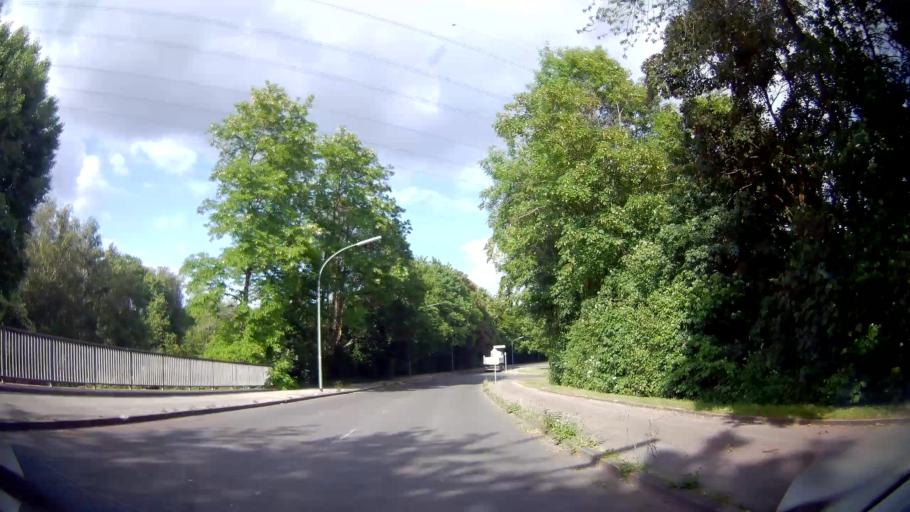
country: DE
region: North Rhine-Westphalia
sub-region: Regierungsbezirk Dusseldorf
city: Essen
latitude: 51.5131
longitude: 7.0498
